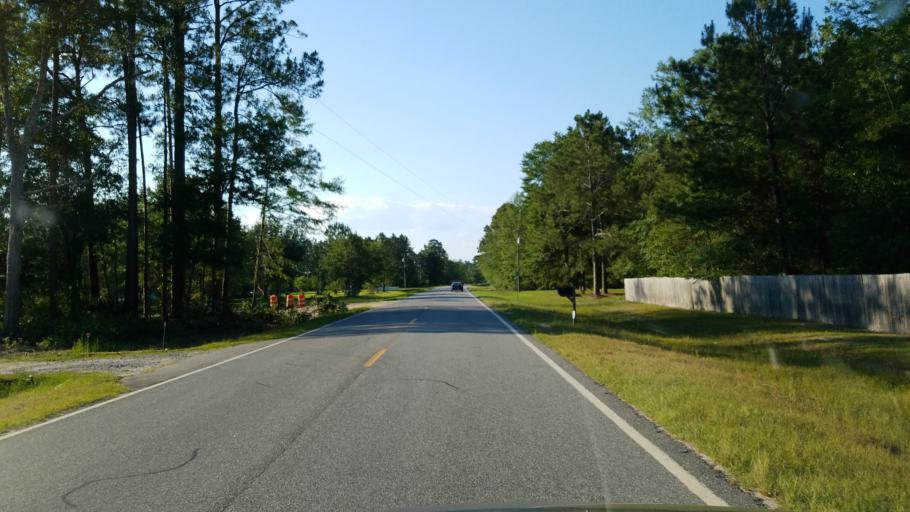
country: US
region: Georgia
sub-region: Lanier County
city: Lakeland
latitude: 30.9232
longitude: -83.0805
